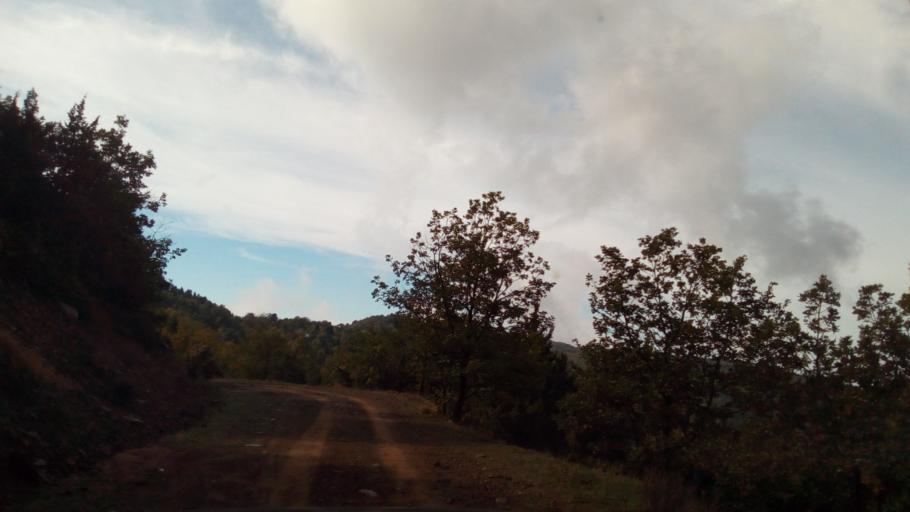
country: GR
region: Central Greece
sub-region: Nomos Fokidos
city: Lidoriki
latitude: 38.4793
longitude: 22.0504
